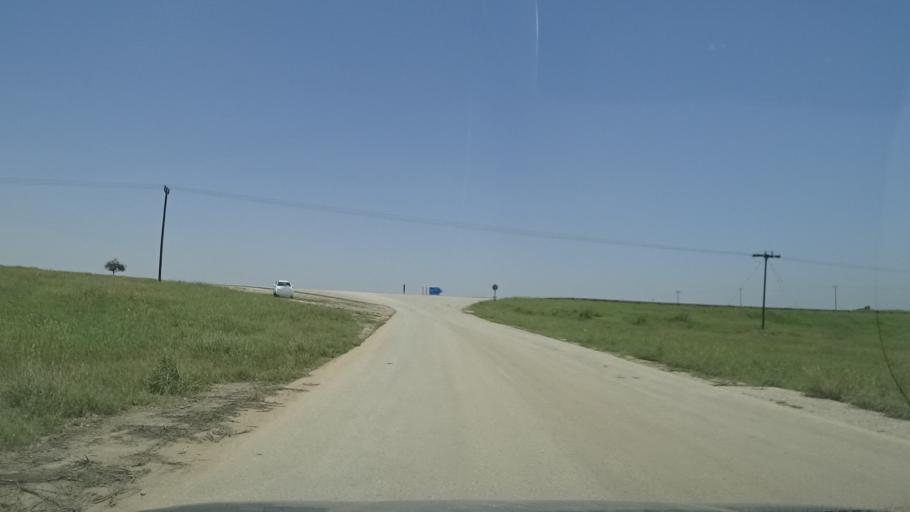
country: OM
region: Zufar
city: Salalah
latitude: 17.2503
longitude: 54.2757
